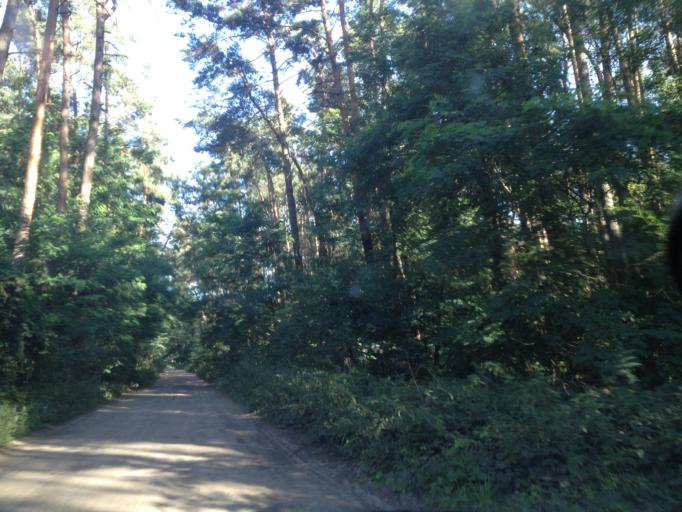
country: PL
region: Greater Poland Voivodeship
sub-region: Powiat sredzki
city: Zaniemysl
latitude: 52.1073
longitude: 17.1265
